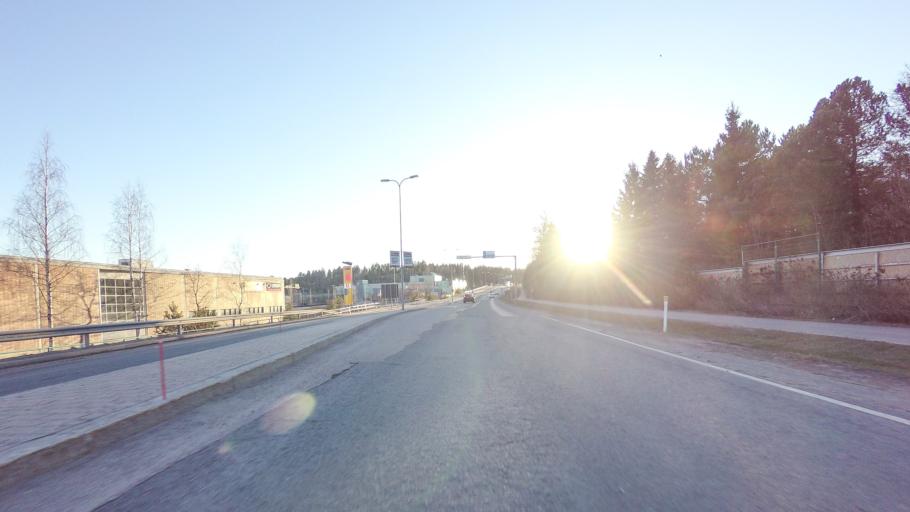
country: FI
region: Uusimaa
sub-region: Helsinki
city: Vantaa
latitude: 60.2816
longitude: 25.0866
